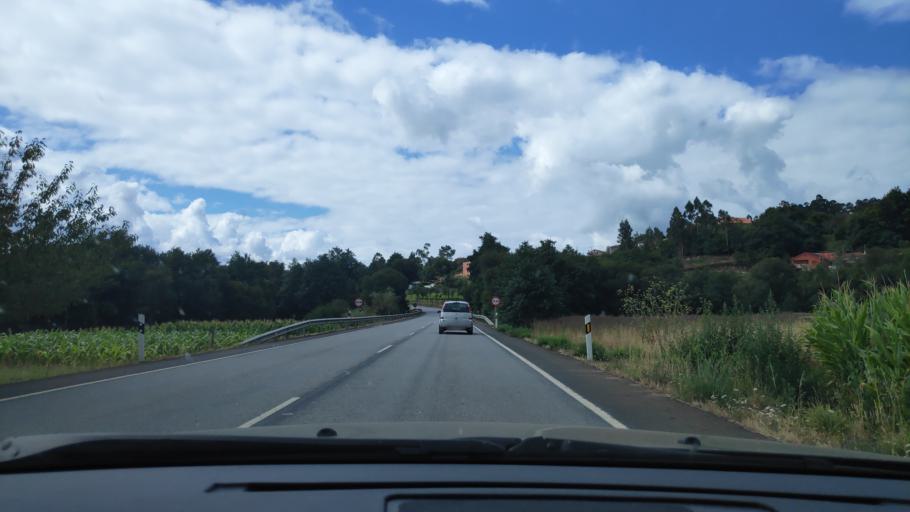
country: ES
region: Galicia
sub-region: Provincia de Pontevedra
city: Portas
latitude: 42.5920
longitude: -8.6906
